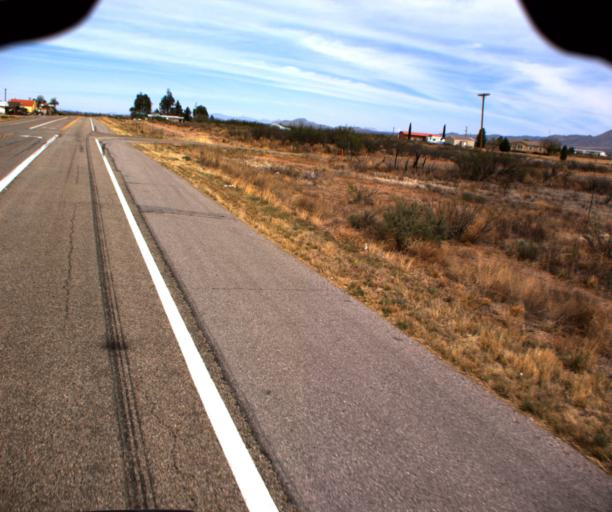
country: US
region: Arizona
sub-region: Cochise County
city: Pirtleville
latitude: 31.5979
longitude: -109.6699
